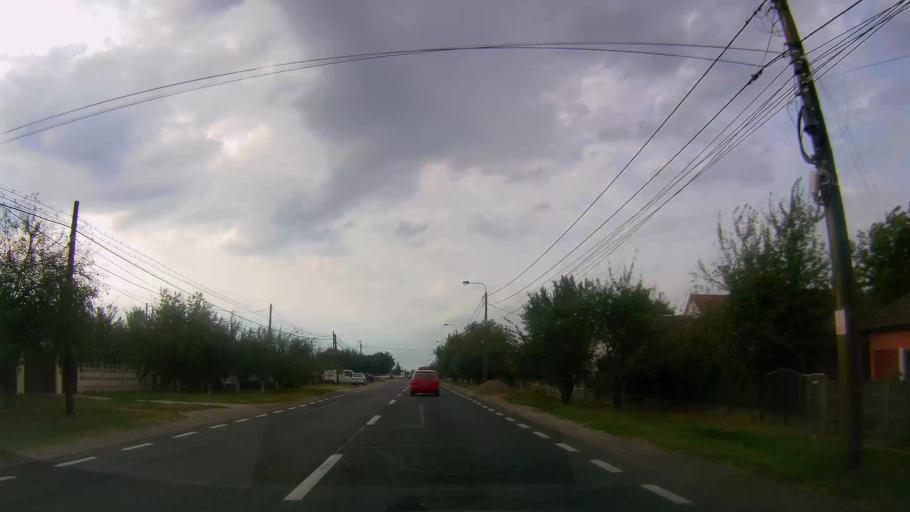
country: RO
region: Satu Mare
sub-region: Comuna Paulesti
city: Paulesti
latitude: 47.7385
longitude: 22.8826
